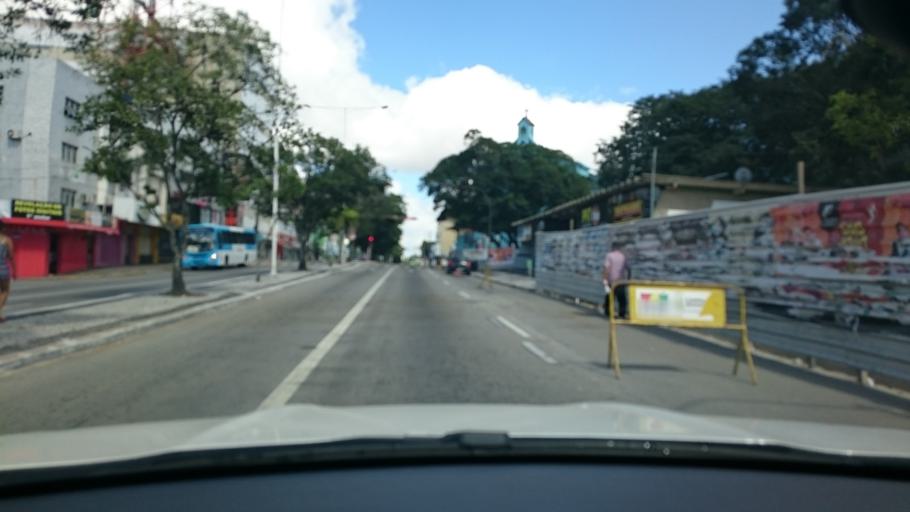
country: BR
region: Paraiba
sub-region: Campina Grande
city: Campina Grande
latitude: -7.2197
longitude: -35.8845
